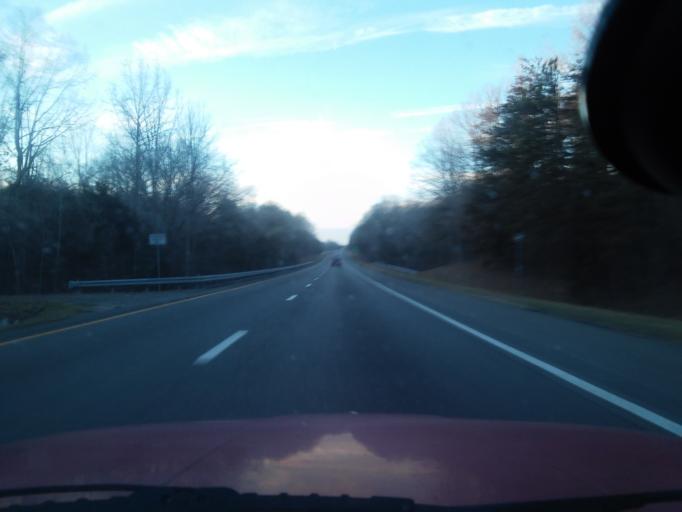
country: US
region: Virginia
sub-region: Goochland County
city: Goochland
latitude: 37.8374
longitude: -77.9737
